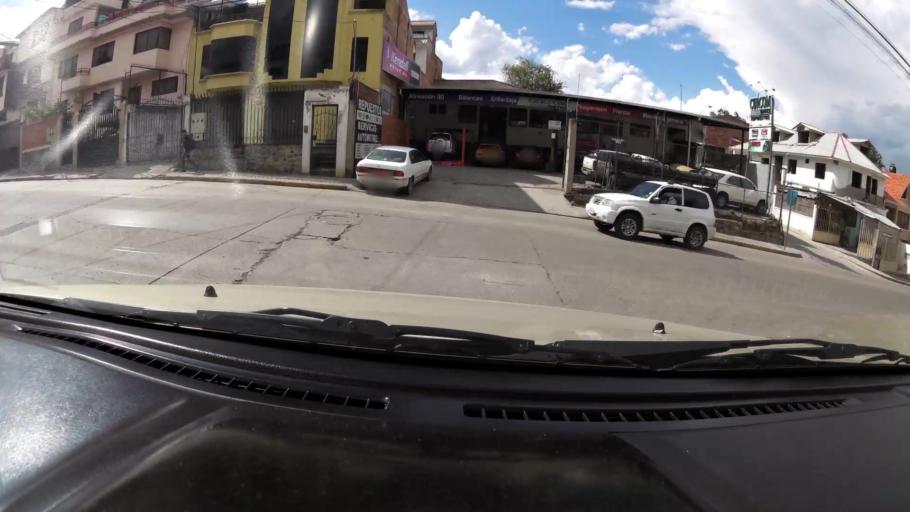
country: EC
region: Azuay
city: Cuenca
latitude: -2.8861
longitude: -78.9921
